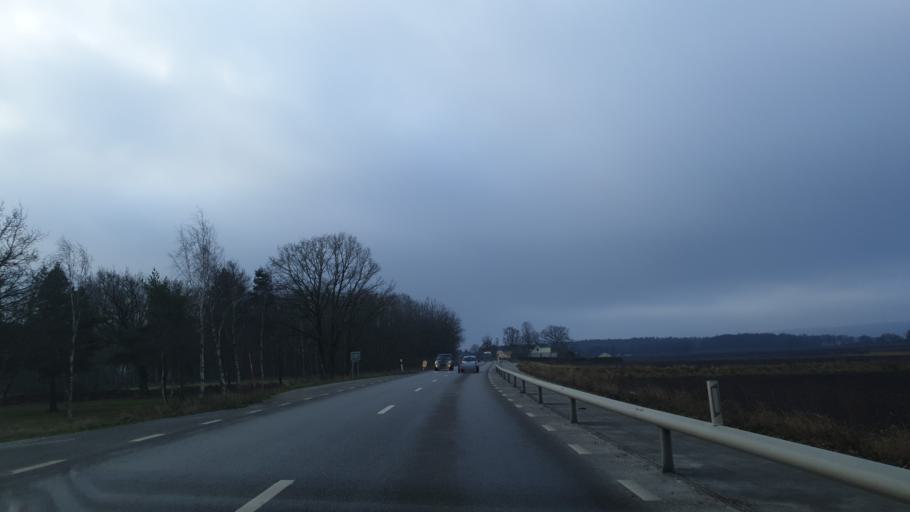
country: SE
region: Blekinge
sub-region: Karlshamns Kommun
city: Morrum
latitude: 56.1076
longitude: 14.6733
